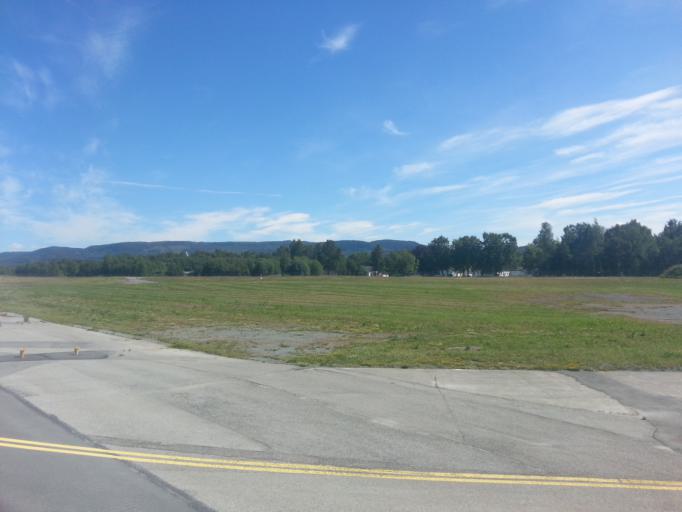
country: NO
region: Nord-Trondelag
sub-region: Stjordal
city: Stjordalshalsen
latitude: 63.4573
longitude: 10.9414
